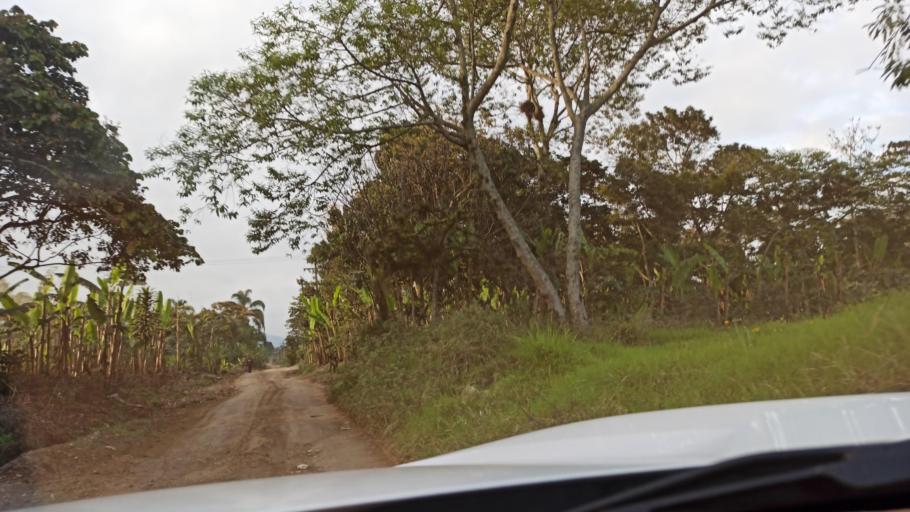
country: MX
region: Veracruz
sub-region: Fortin
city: Fortin de las Flores
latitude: 18.9181
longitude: -97.0033
